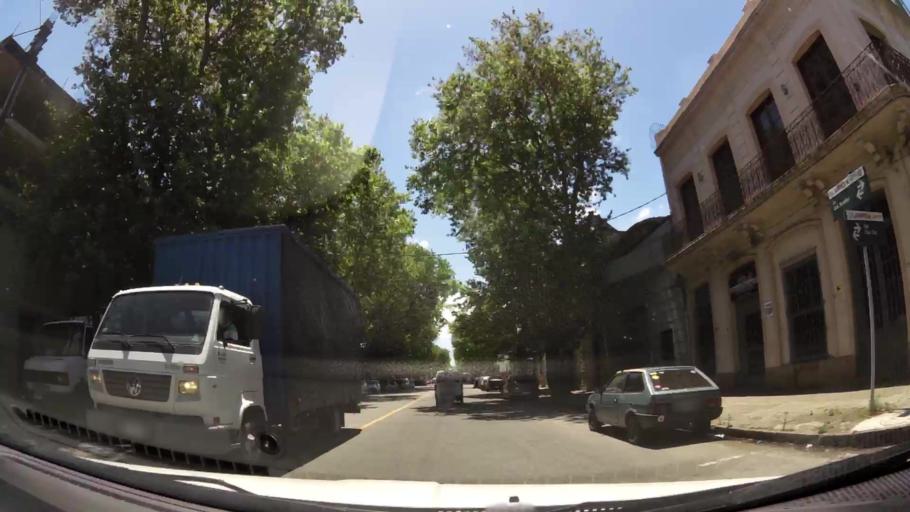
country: UY
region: Montevideo
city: Montevideo
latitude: -34.8894
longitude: -56.1931
